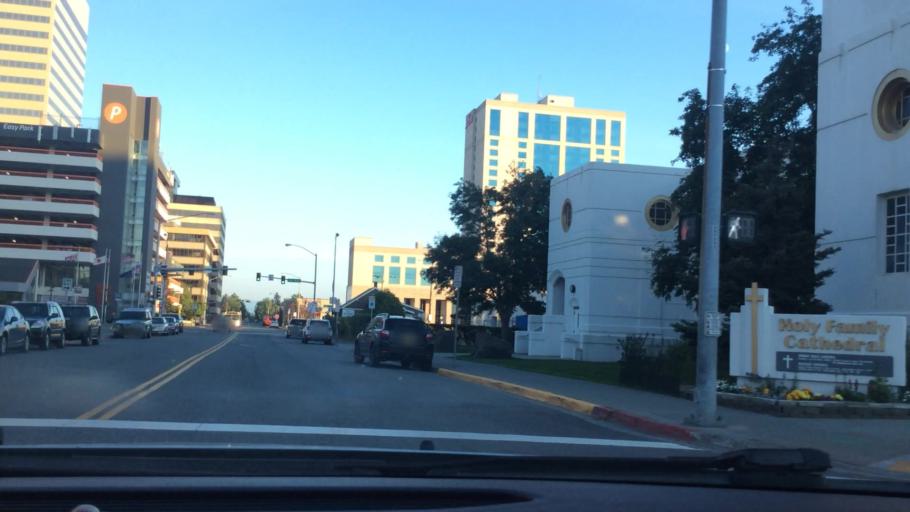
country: US
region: Alaska
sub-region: Anchorage Municipality
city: Anchorage
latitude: 61.2175
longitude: -149.8975
